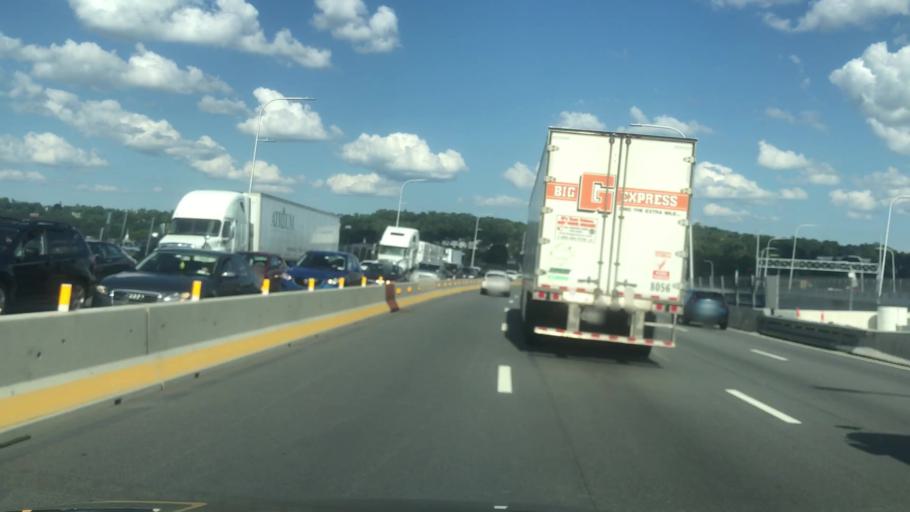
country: US
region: New York
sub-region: Westchester County
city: Tarrytown
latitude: 41.0721
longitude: -73.8751
